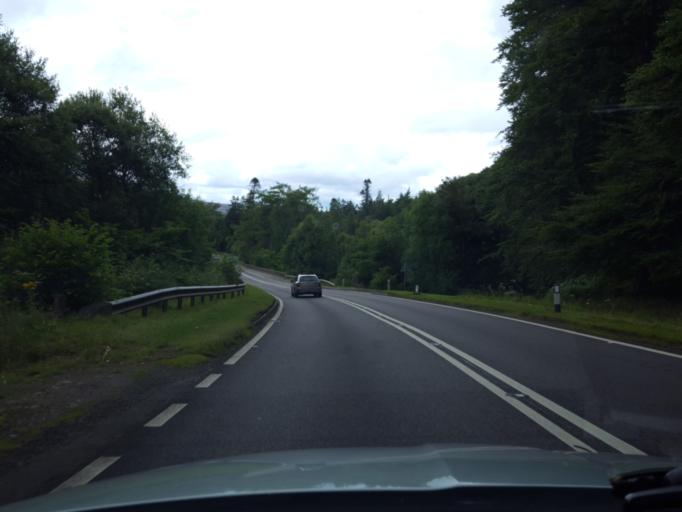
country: GB
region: Scotland
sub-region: Moray
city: Rothes
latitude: 57.4042
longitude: -3.3594
